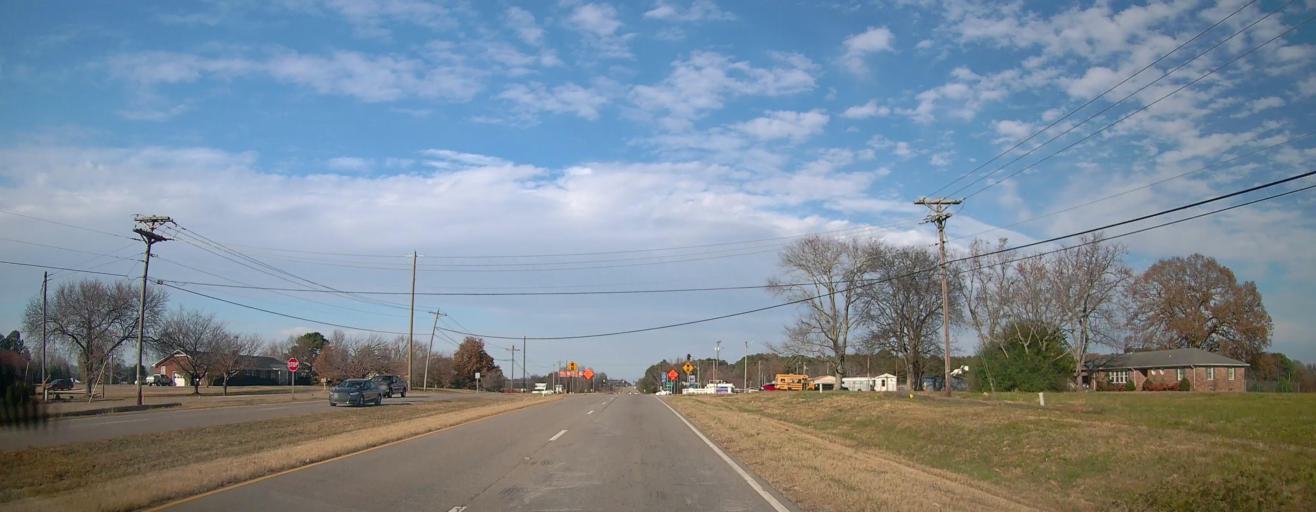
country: US
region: Alabama
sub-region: Limestone County
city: Athens
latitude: 34.7283
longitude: -86.9570
